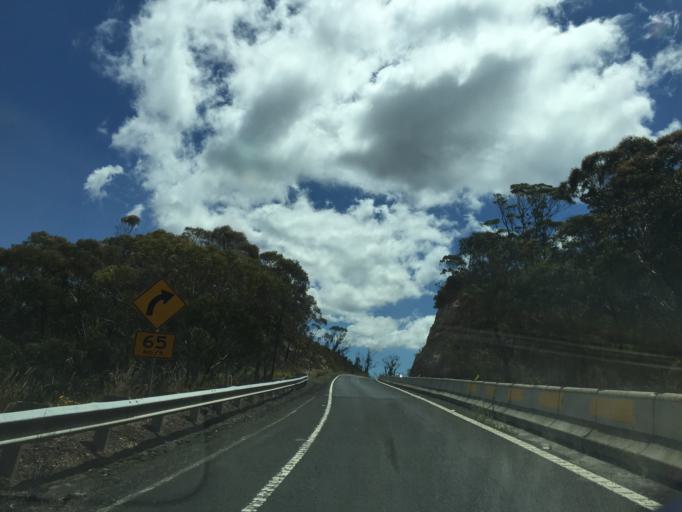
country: AU
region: New South Wales
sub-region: Blue Mountains Municipality
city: Blackheath
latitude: -33.5252
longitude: 150.3091
